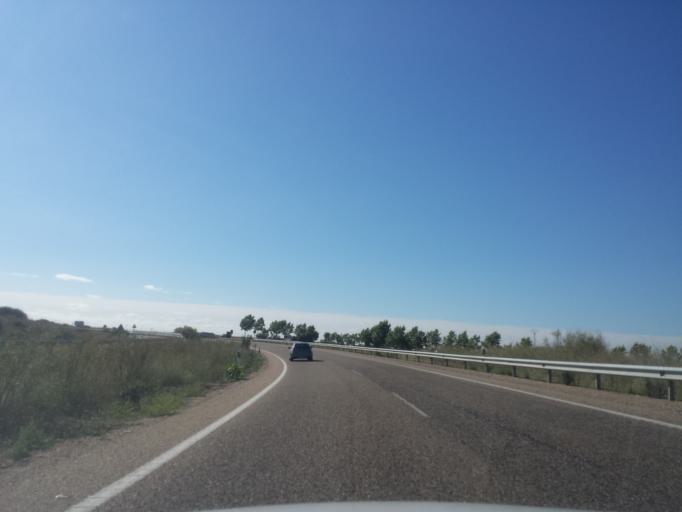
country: ES
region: Castille and Leon
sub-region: Provincia de Zamora
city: Villabrazaro
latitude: 42.0572
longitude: -5.6831
